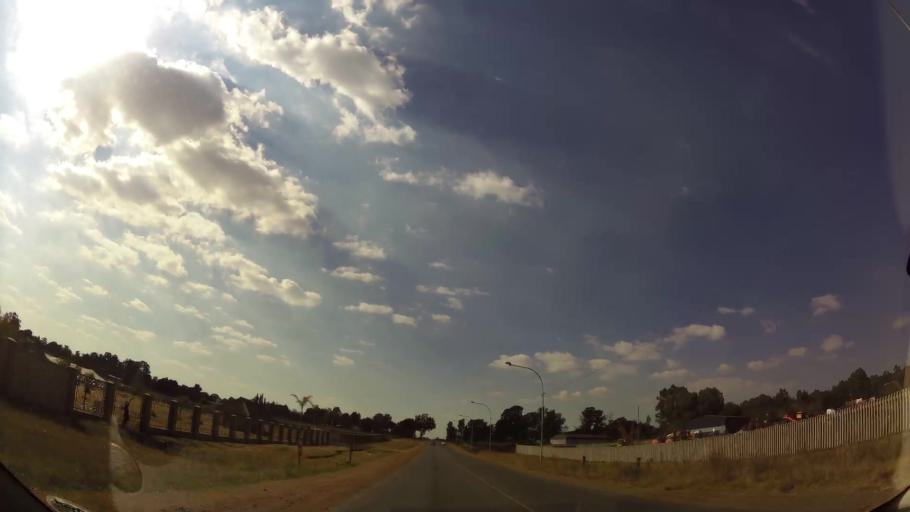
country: ZA
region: Gauteng
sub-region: Ekurhuleni Metropolitan Municipality
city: Benoni
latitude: -26.1024
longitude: 28.3441
